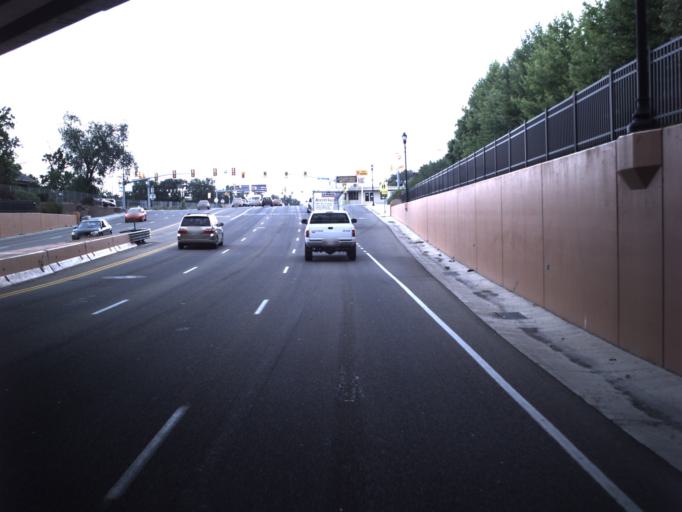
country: US
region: Utah
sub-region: Salt Lake County
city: Midvale
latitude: 40.6081
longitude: -111.8905
